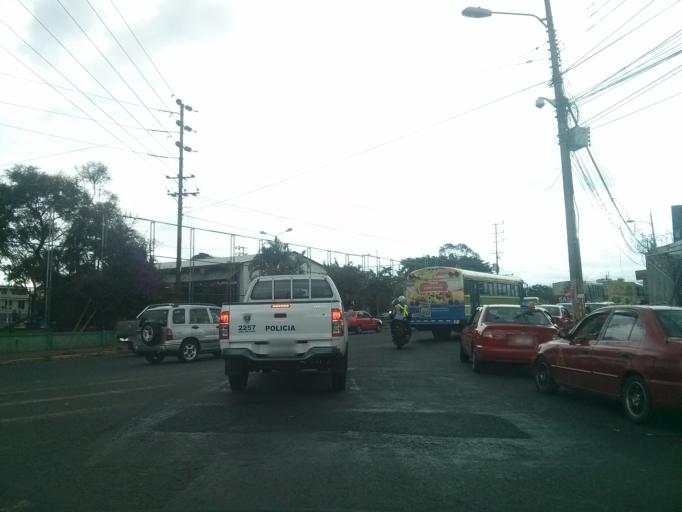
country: CR
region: San Jose
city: San Jose
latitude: 9.9236
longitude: -84.0734
